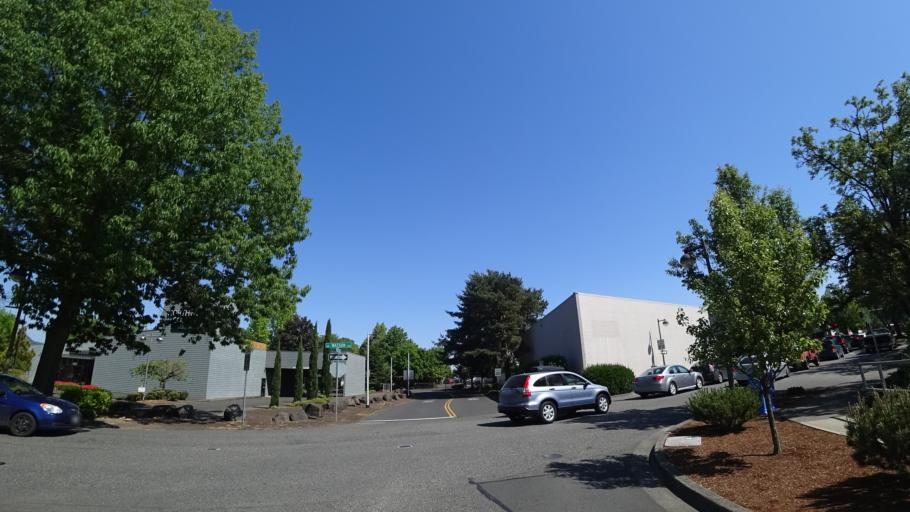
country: US
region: Oregon
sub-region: Washington County
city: Beaverton
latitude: 45.4892
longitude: -122.8064
